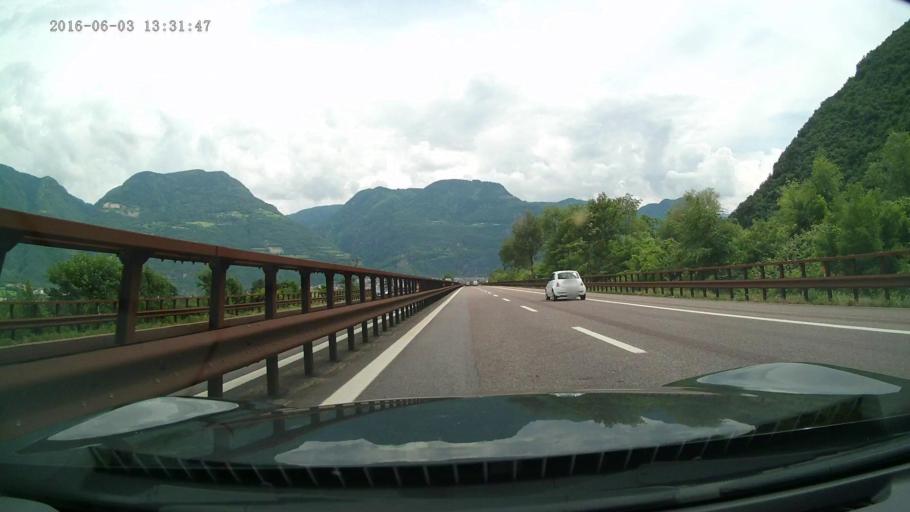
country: IT
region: Trentino-Alto Adige
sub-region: Bolzano
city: San Giacomo
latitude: 46.4462
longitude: 11.3122
